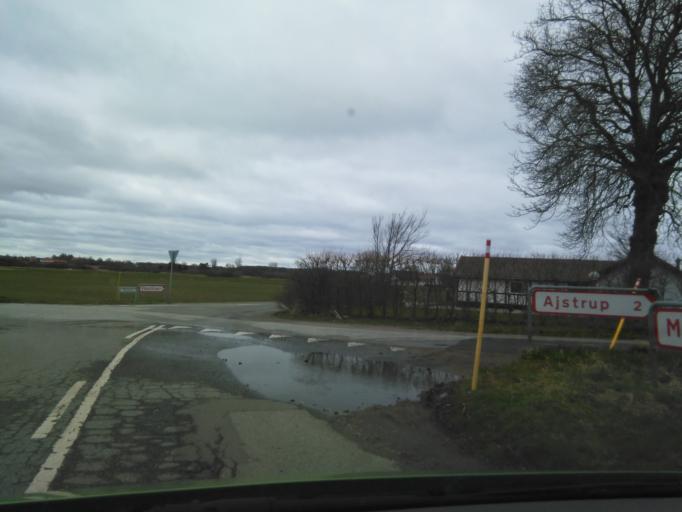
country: DK
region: Central Jutland
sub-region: Arhus Kommune
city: Beder
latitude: 56.0482
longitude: 10.2185
